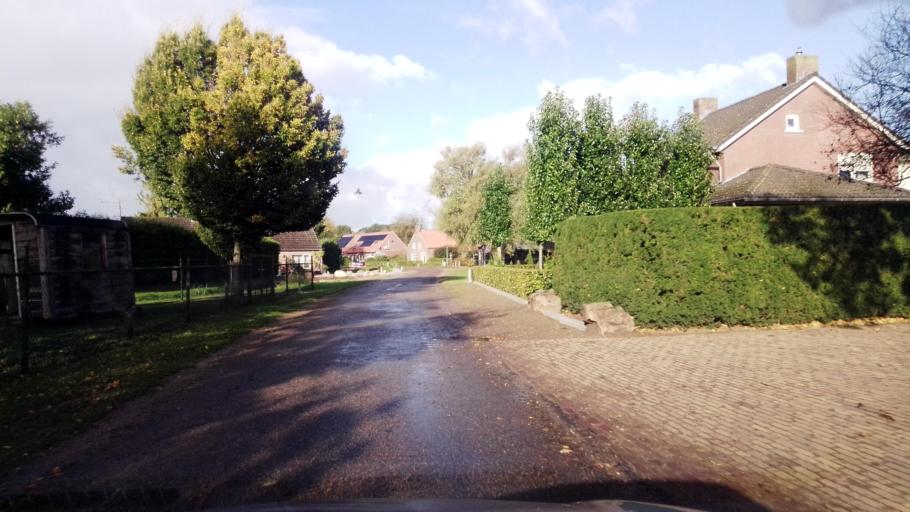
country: NL
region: Limburg
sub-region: Gemeente Peel en Maas
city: Maasbree
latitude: 51.3398
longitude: 6.0784
